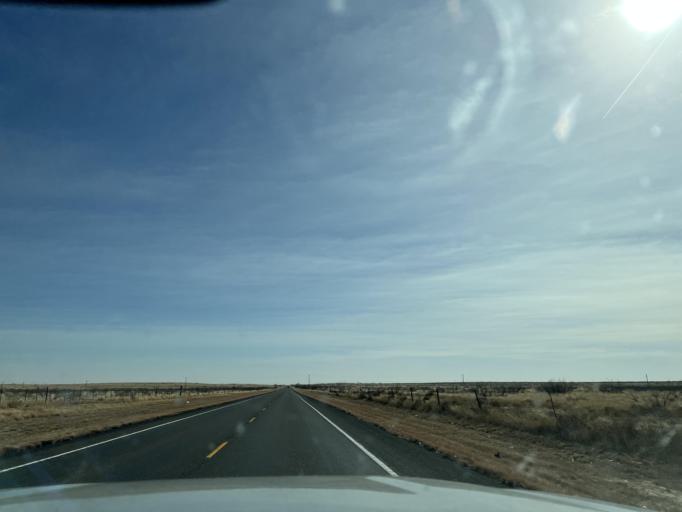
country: US
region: Texas
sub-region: Andrews County
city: Andrews
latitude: 32.4835
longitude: -102.4789
